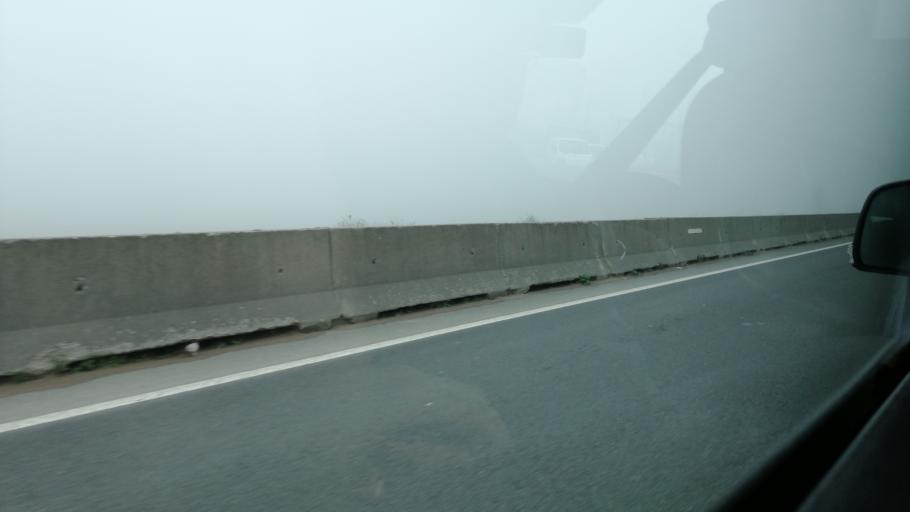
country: TR
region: Yalova
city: Taskopru
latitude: 40.6801
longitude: 29.3696
